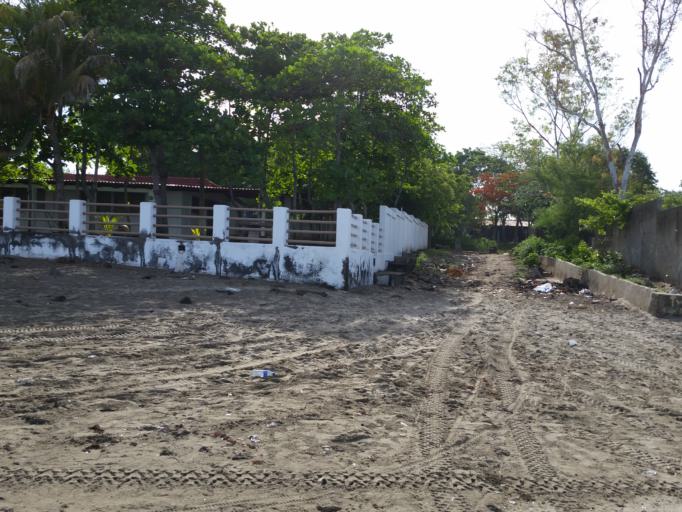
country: NI
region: Managua
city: Masachapa
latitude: 11.7808
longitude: -86.5190
